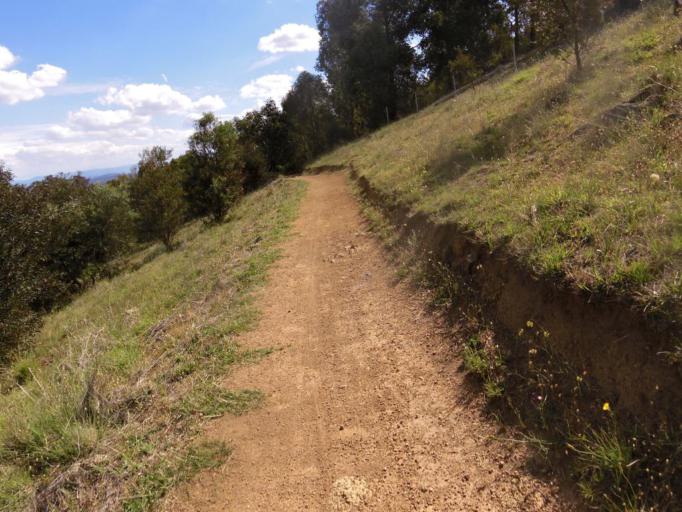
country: AU
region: Australian Capital Territory
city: Belconnen
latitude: -35.1526
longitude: 149.0865
